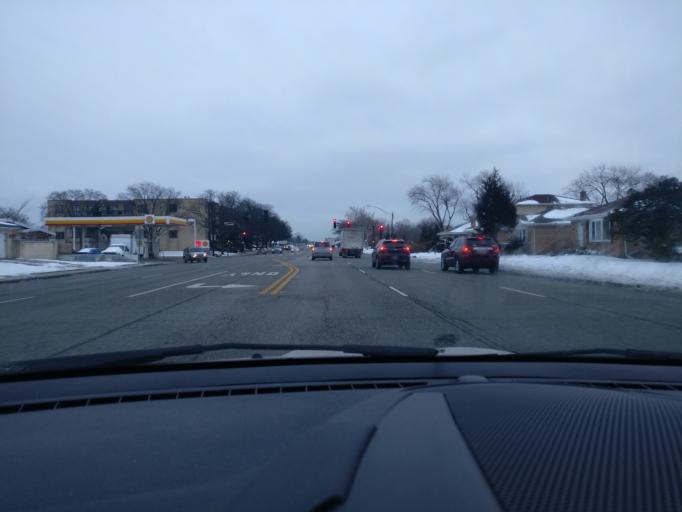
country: US
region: Illinois
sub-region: Cook County
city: Niles
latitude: 42.0404
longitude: -87.8211
